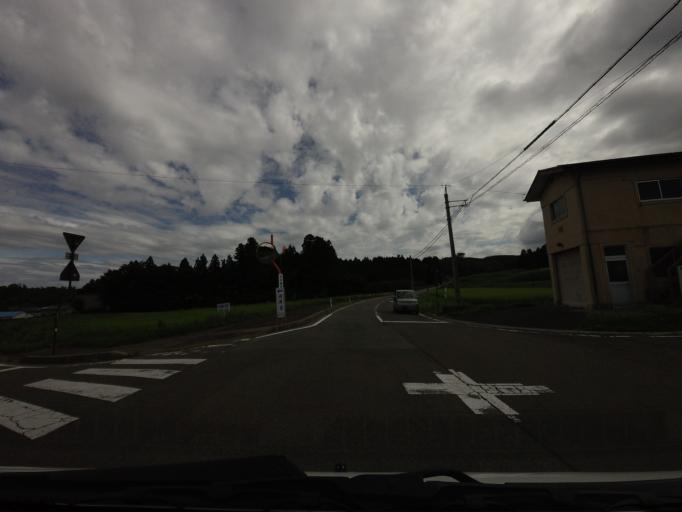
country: JP
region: Fukushima
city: Nihommatsu
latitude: 37.6582
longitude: 140.4242
